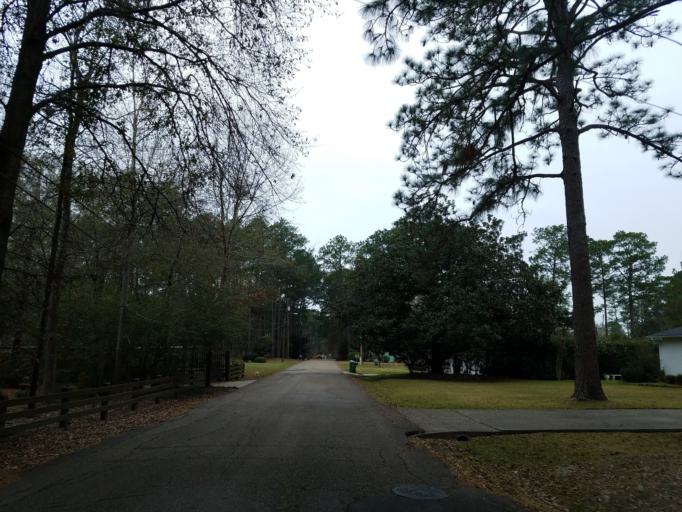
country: US
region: Mississippi
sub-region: Forrest County
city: Hattiesburg
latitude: 31.3137
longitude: -89.3207
